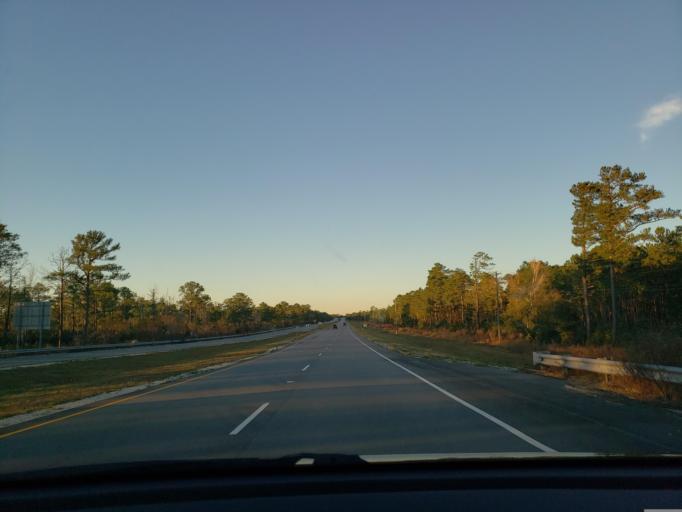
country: US
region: North Carolina
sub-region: Onslow County
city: Sneads Ferry
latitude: 34.5973
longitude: -77.4810
